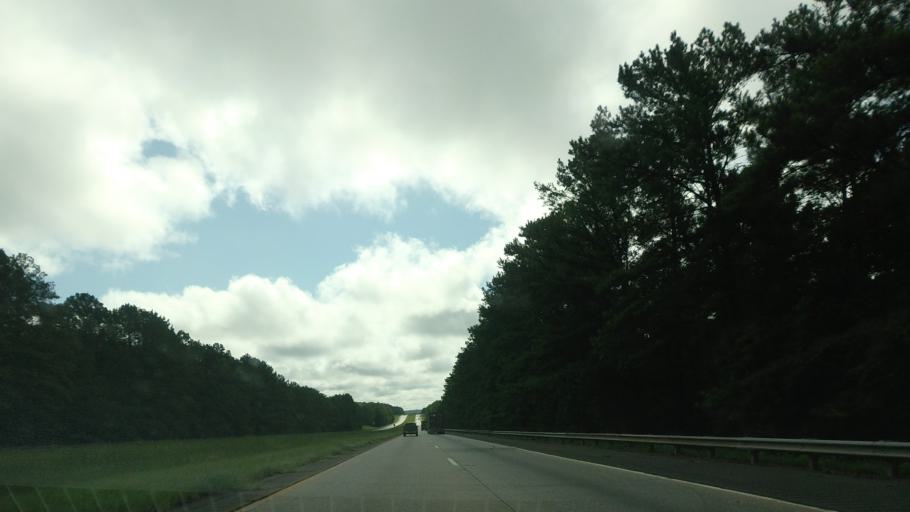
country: US
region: Georgia
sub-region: Twiggs County
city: Jeffersonville
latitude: 32.6660
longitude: -83.4619
